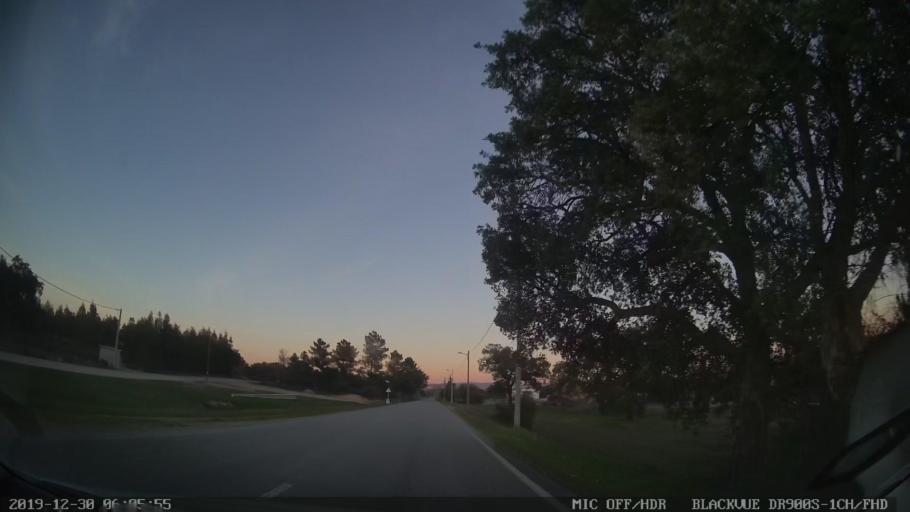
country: PT
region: Castelo Branco
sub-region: Penamacor
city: Penamacor
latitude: 40.0943
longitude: -7.2348
